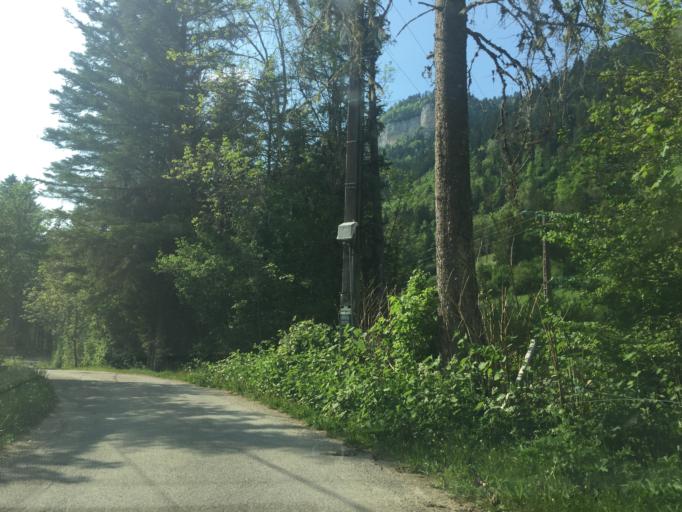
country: FR
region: Rhone-Alpes
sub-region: Departement de l'Isere
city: Saint-Hilaire
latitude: 45.3322
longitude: 5.8440
